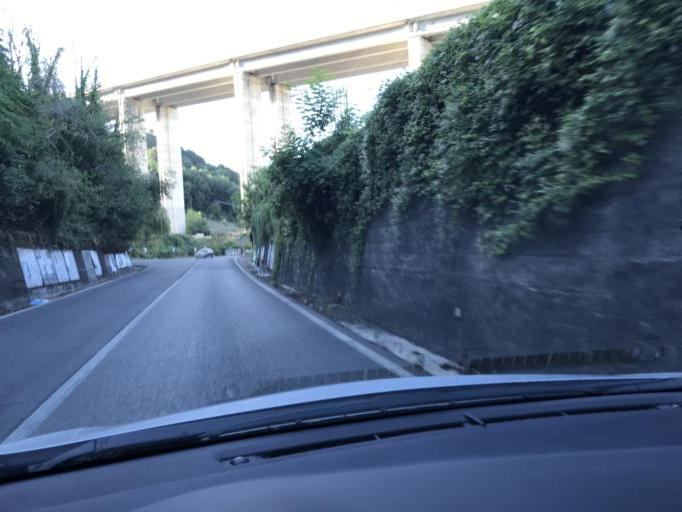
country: IT
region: Latium
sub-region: Provincia di Viterbo
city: Orte
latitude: 42.4504
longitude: 12.3889
